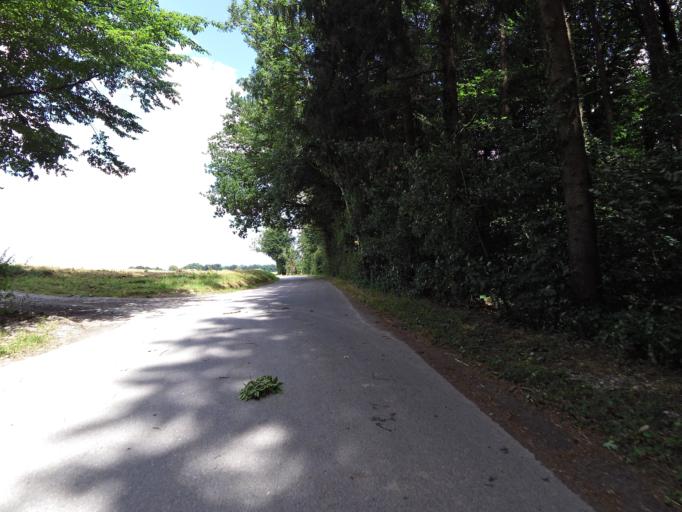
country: CH
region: Thurgau
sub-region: Kreuzlingen District
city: Ermatingen
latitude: 47.6479
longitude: 9.0887
